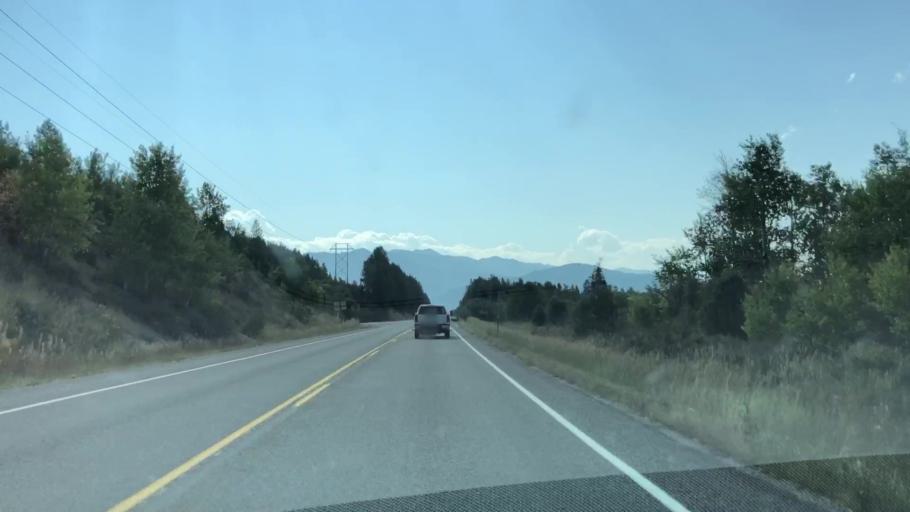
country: US
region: Wyoming
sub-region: Teton County
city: Hoback
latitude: 43.2024
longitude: -111.0456
